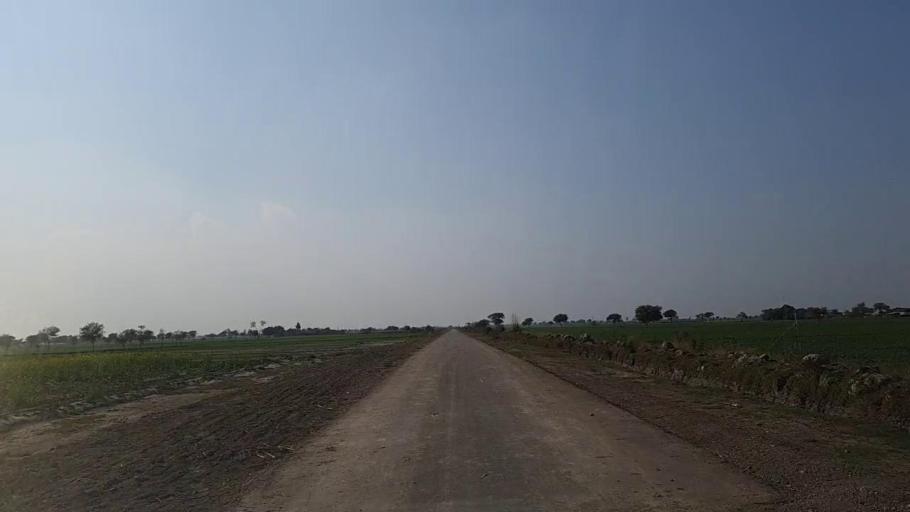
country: PK
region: Sindh
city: Jam Sahib
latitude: 26.3000
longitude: 68.5827
